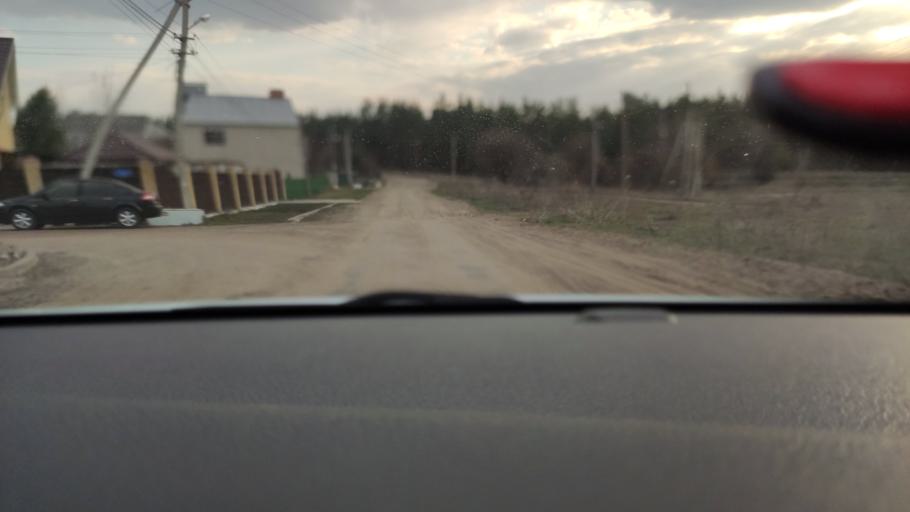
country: RU
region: Voronezj
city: Pridonskoy
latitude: 51.6340
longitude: 39.0864
